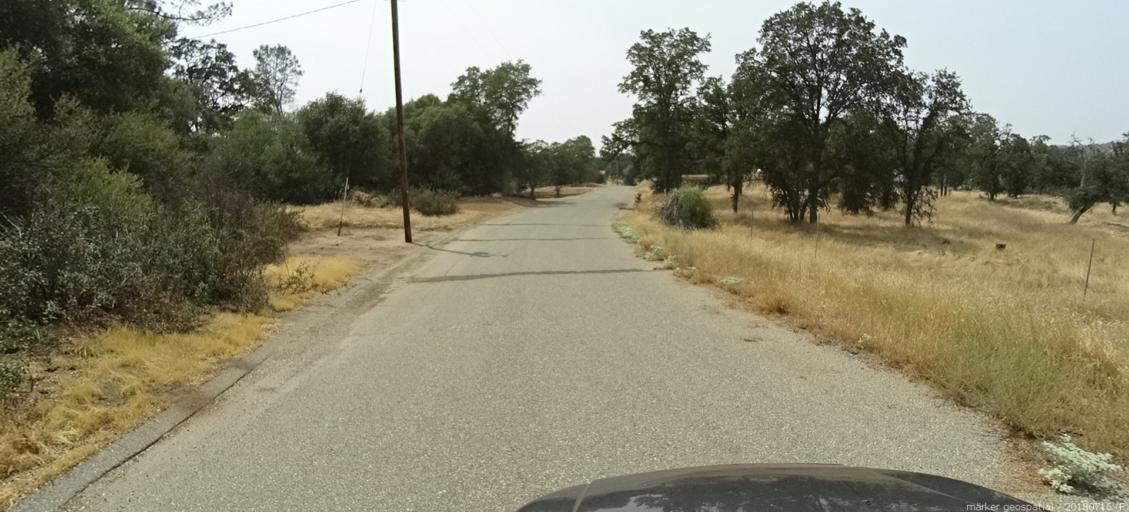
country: US
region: California
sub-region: Madera County
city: Yosemite Lakes
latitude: 37.2161
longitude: -119.7781
